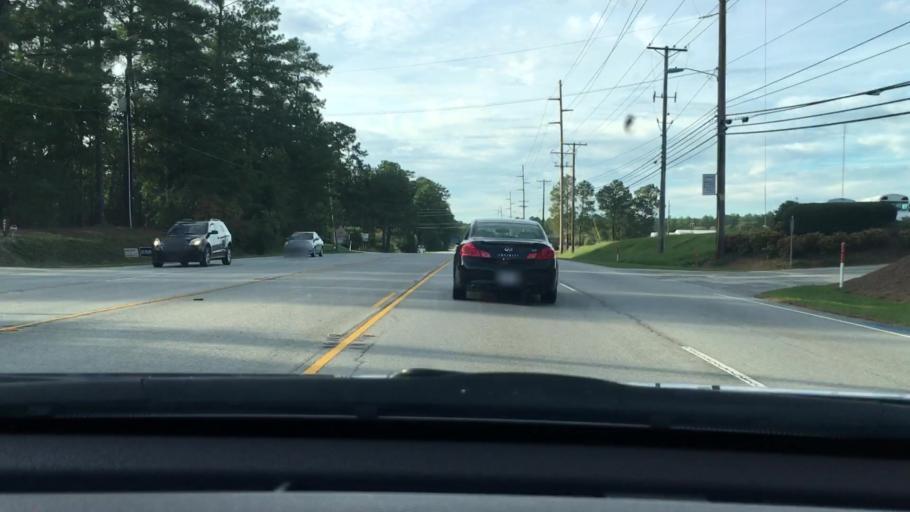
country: US
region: South Carolina
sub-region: Lexington County
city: Saint Andrews
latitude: 34.0724
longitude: -81.1220
